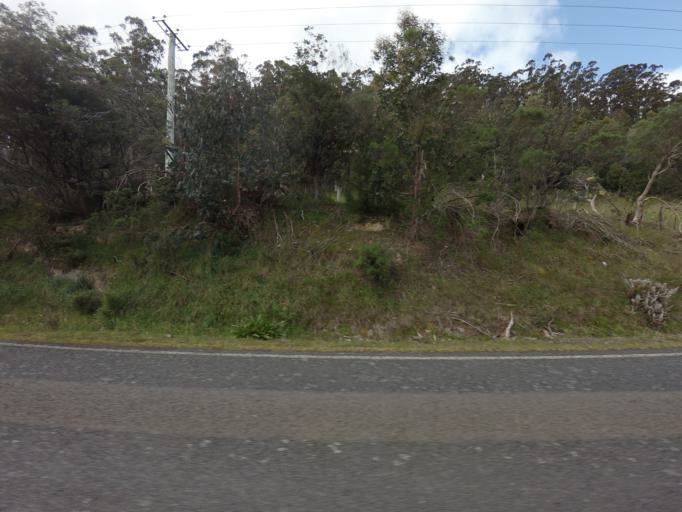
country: AU
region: Tasmania
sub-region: Huon Valley
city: Cygnet
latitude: -43.2801
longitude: 147.0100
